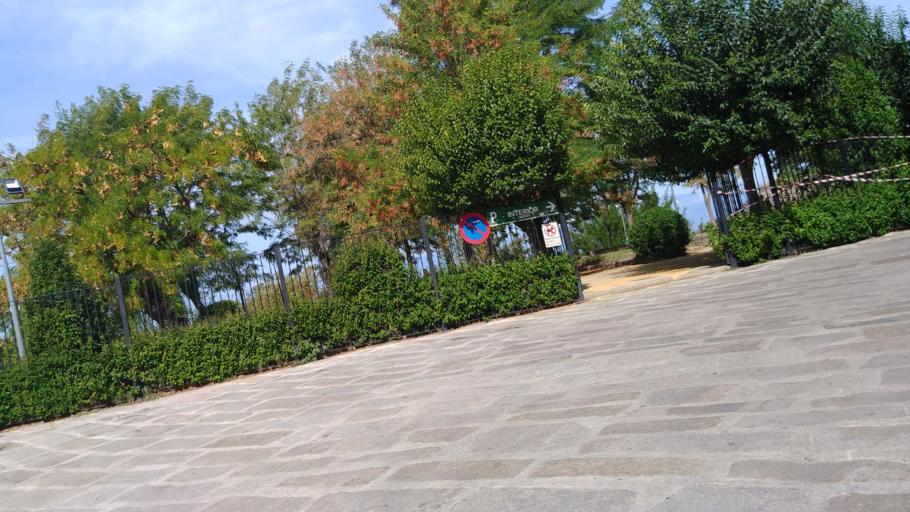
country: ES
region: Castille-La Mancha
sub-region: Province of Toledo
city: Oropesa
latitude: 39.9193
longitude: -5.1749
